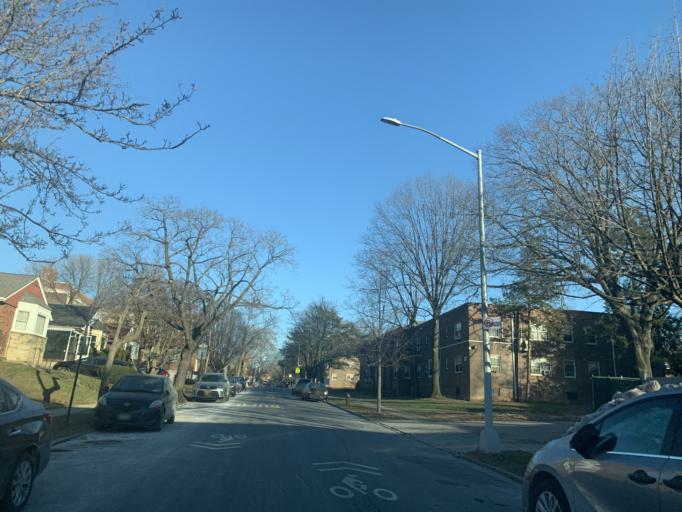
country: US
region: New York
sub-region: Queens County
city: Jamaica
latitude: 40.7207
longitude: -73.8247
